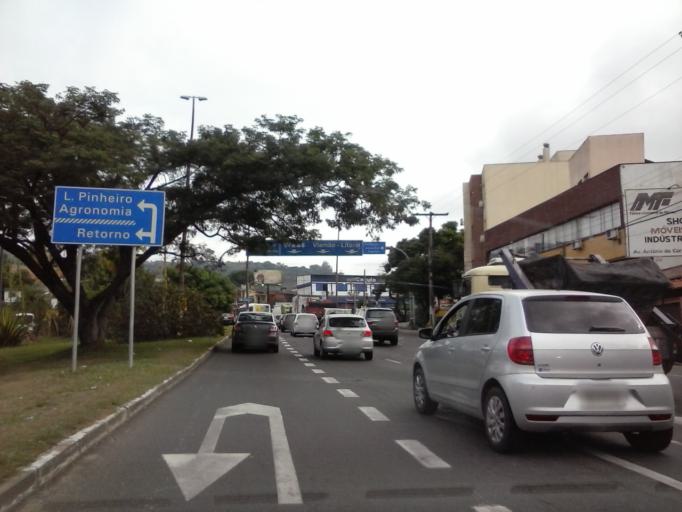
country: BR
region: Rio Grande do Sul
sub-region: Porto Alegre
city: Porto Alegre
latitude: -30.0647
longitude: -51.1508
